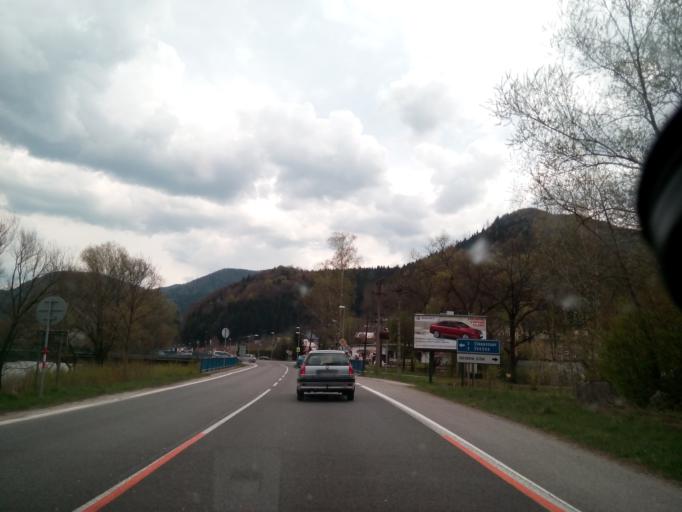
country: SK
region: Zilinsky
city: Ruzomberok
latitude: 49.1235
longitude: 19.1689
